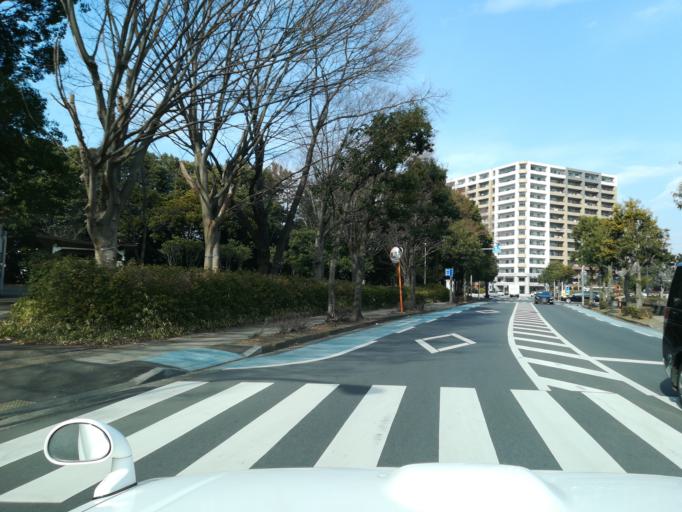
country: JP
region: Ibaraki
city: Naka
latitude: 36.0849
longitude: 140.1080
